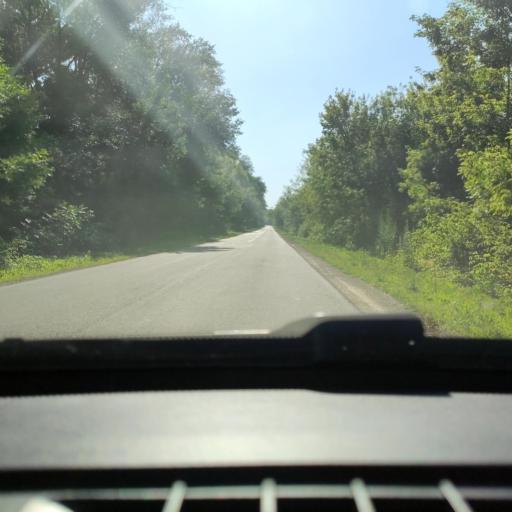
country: RU
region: Voronezj
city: Panino
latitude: 51.6173
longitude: 40.2113
